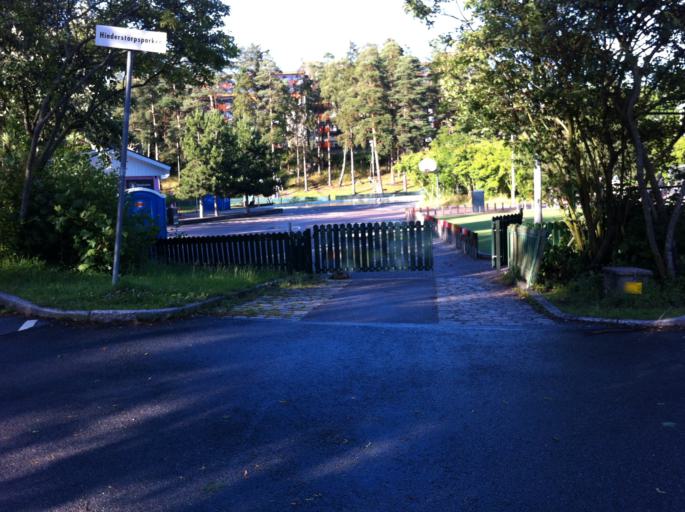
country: SE
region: Stockholm
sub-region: Stockholms Kommun
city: Kista
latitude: 59.3888
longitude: 17.9330
